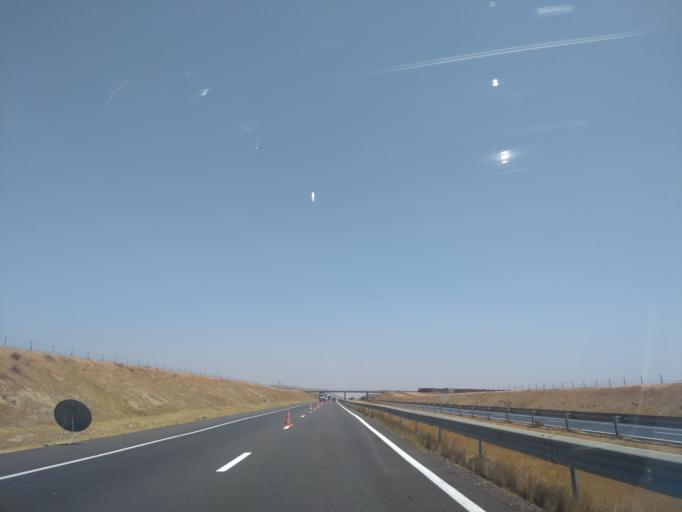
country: MA
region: Marrakech-Tensift-Al Haouz
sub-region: Kelaa-Des-Sraghna
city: Sidi Abdallah
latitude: 32.4336
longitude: -7.9314
